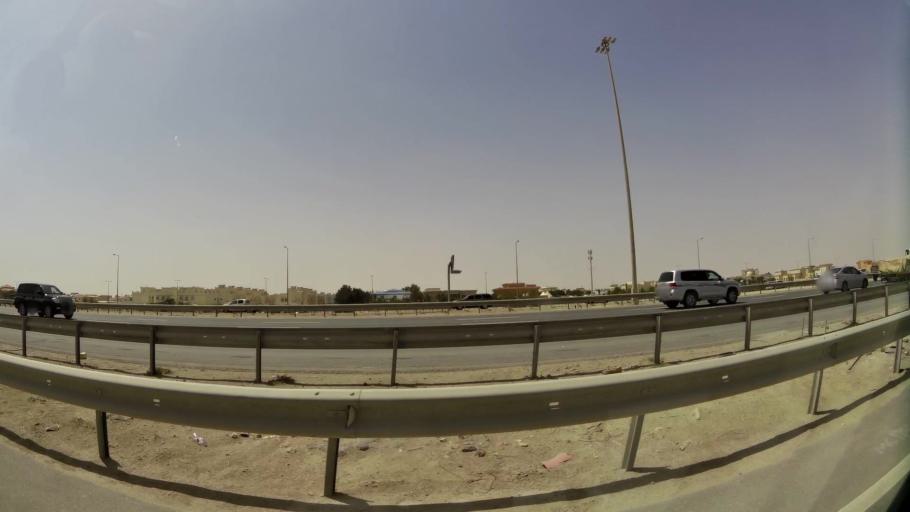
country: QA
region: Baladiyat Umm Salal
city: Umm Salal Muhammad
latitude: 25.3853
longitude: 51.4378
